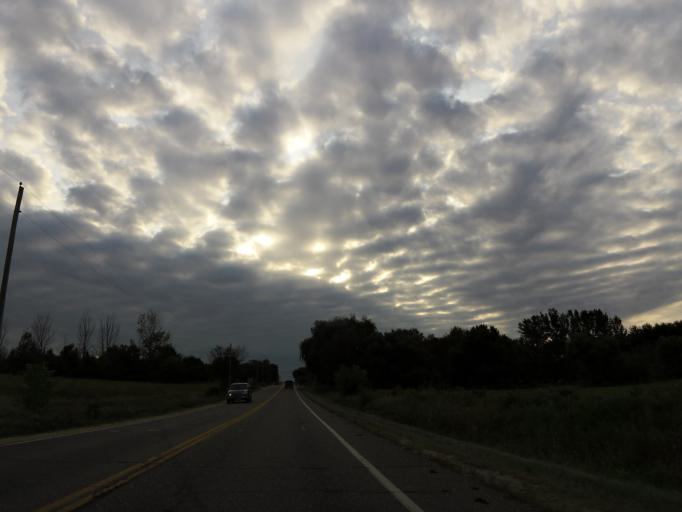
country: US
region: Minnesota
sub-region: Dakota County
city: Lakeville
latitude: 44.6560
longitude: -93.2201
